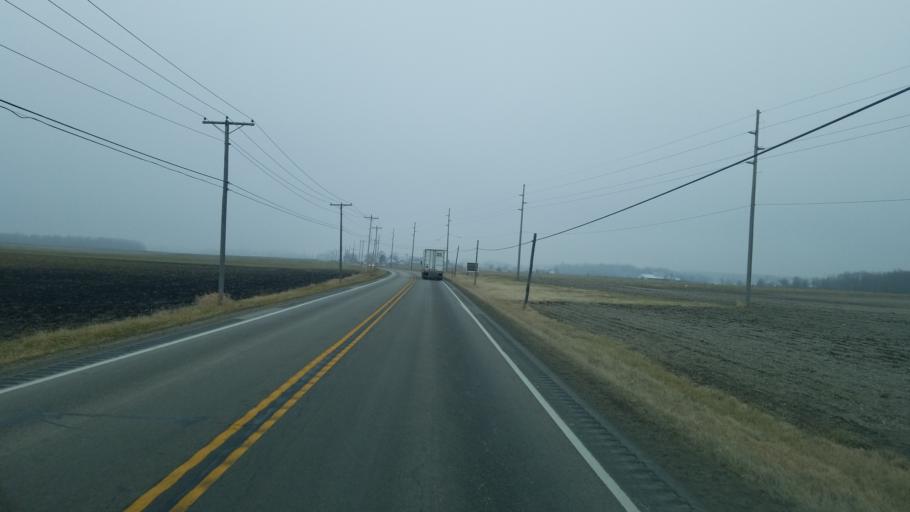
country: US
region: Indiana
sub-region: Adams County
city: Geneva
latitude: 40.5467
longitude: -84.9623
